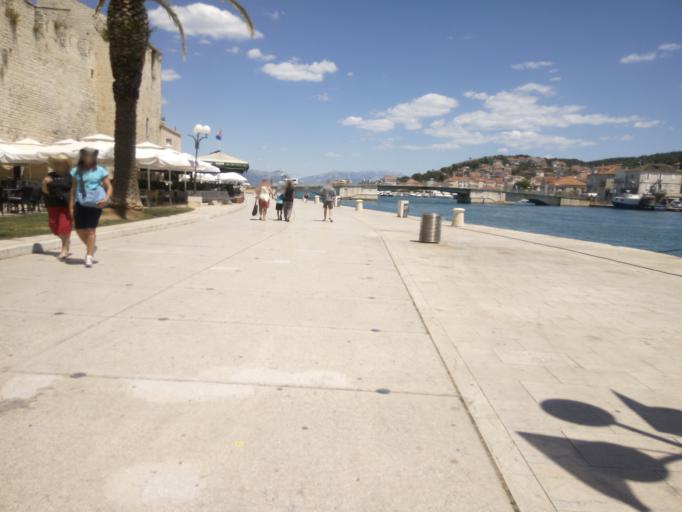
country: HR
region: Splitsko-Dalmatinska
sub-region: Grad Trogir
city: Trogir
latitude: 43.5156
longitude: 16.2501
